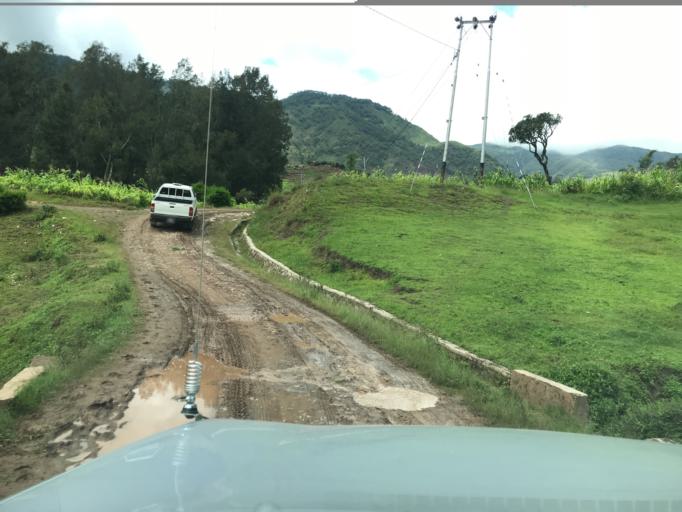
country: TL
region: Aileu
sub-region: Aileu Villa
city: Aileu
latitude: -8.8587
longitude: 125.5732
